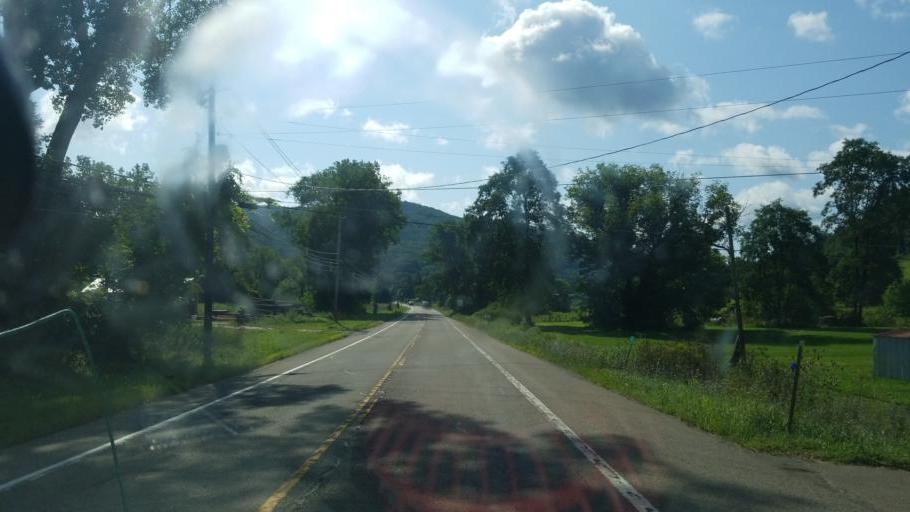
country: US
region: New York
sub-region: Steuben County
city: Canisteo
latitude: 42.2639
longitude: -77.5925
